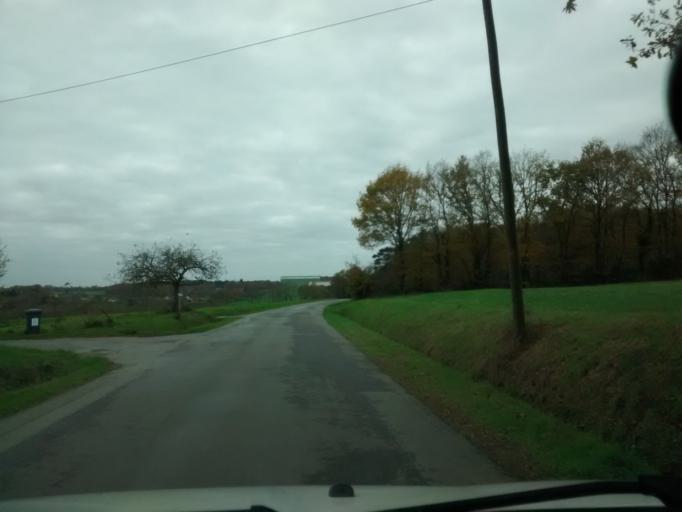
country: FR
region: Brittany
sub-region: Departement d'Ille-et-Vilaine
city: Erbree
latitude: 48.0985
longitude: -1.1495
